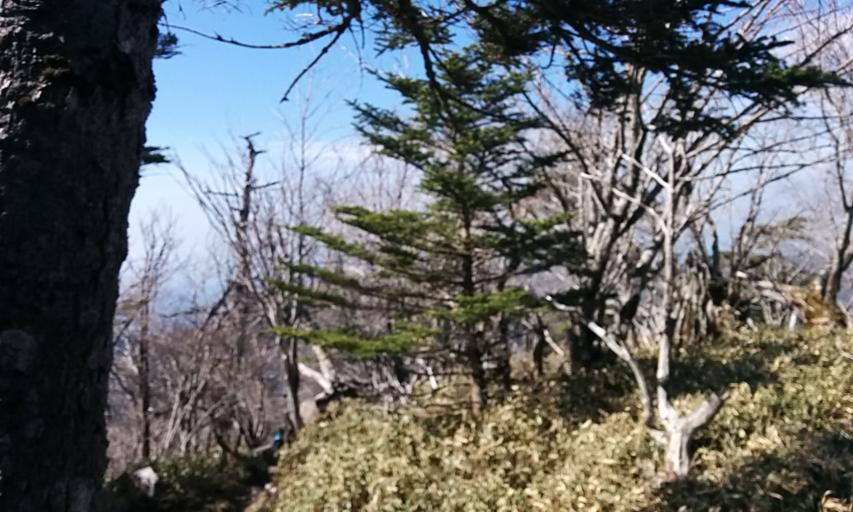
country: JP
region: Tokushima
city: Wakimachi
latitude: 33.8573
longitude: 134.0954
